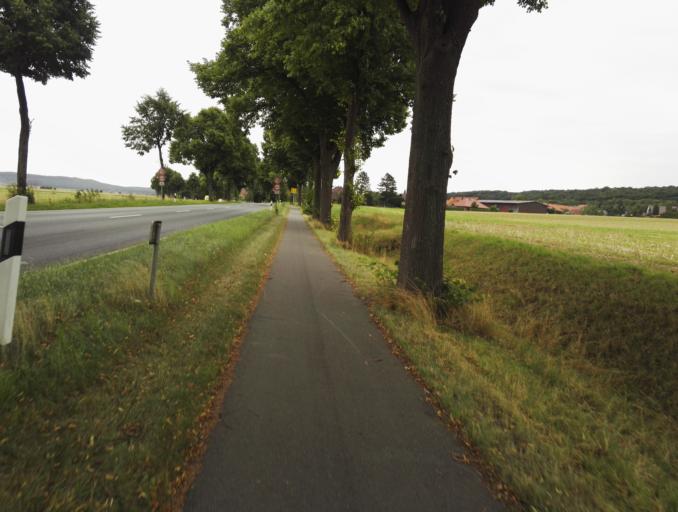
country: DE
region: Lower Saxony
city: Hildesheim
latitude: 52.1406
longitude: 10.0168
